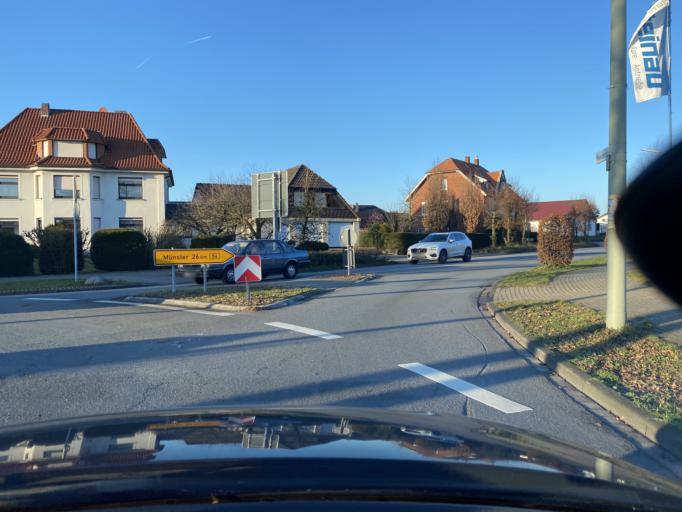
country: DE
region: North Rhine-Westphalia
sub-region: Regierungsbezirk Munster
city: Ascheberg
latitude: 51.7437
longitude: 7.6624
